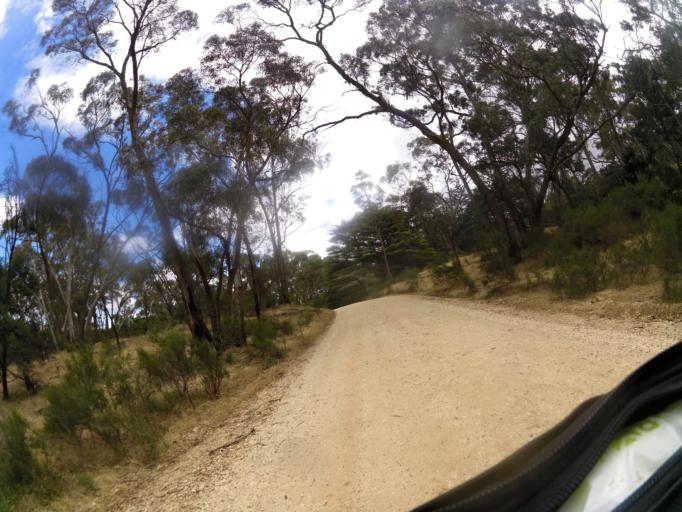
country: AU
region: Victoria
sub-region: Mount Alexander
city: Castlemaine
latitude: -37.0317
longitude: 144.2619
